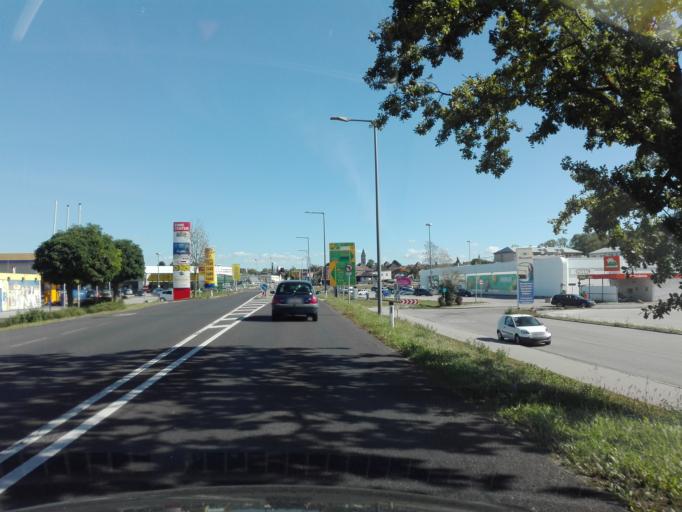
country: AT
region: Upper Austria
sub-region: Politischer Bezirk Linz-Land
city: Enns
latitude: 48.2159
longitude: 14.4625
